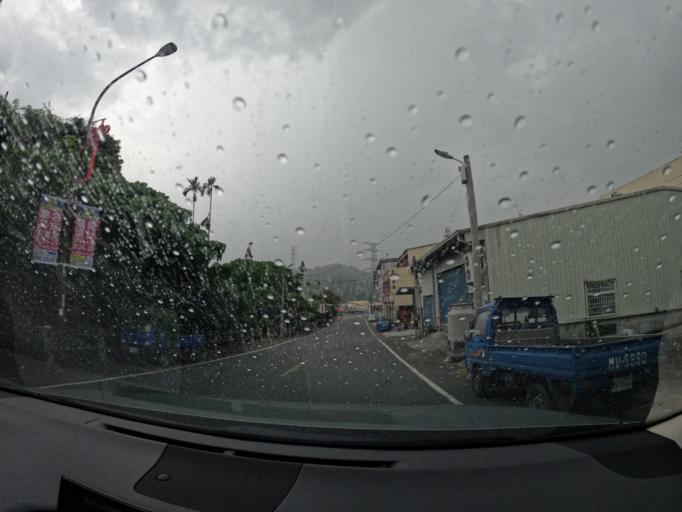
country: TW
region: Taiwan
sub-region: Nantou
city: Nantou
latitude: 23.8806
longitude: 120.7629
